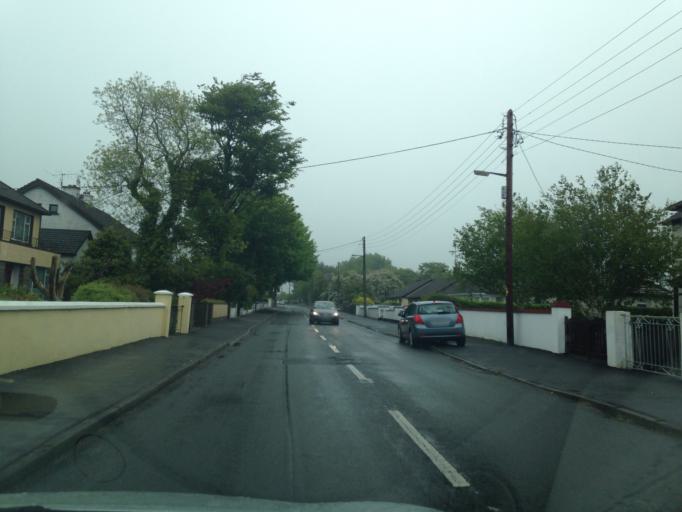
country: IE
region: Connaught
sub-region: County Galway
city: Gaillimh
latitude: 53.2757
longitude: -9.0257
